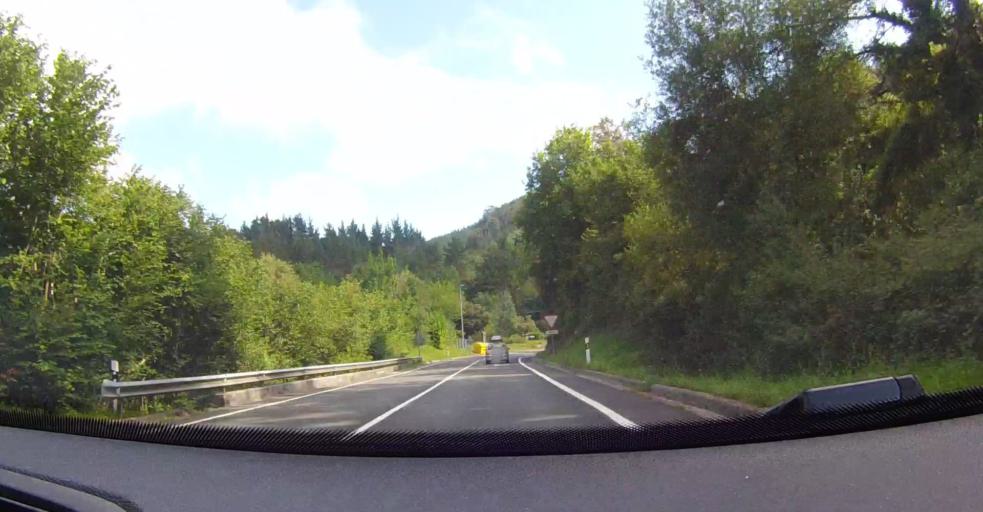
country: ES
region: Basque Country
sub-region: Bizkaia
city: Kortezubi
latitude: 43.3606
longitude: -2.6384
